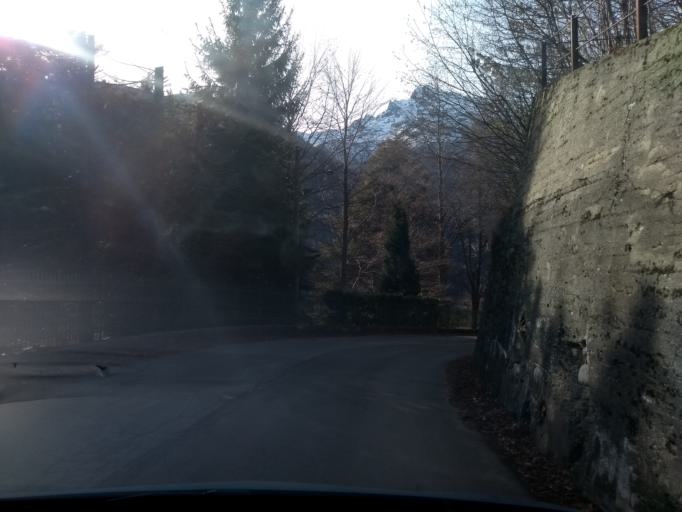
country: IT
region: Piedmont
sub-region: Provincia di Torino
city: Ala di Stura
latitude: 45.3169
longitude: 7.3069
